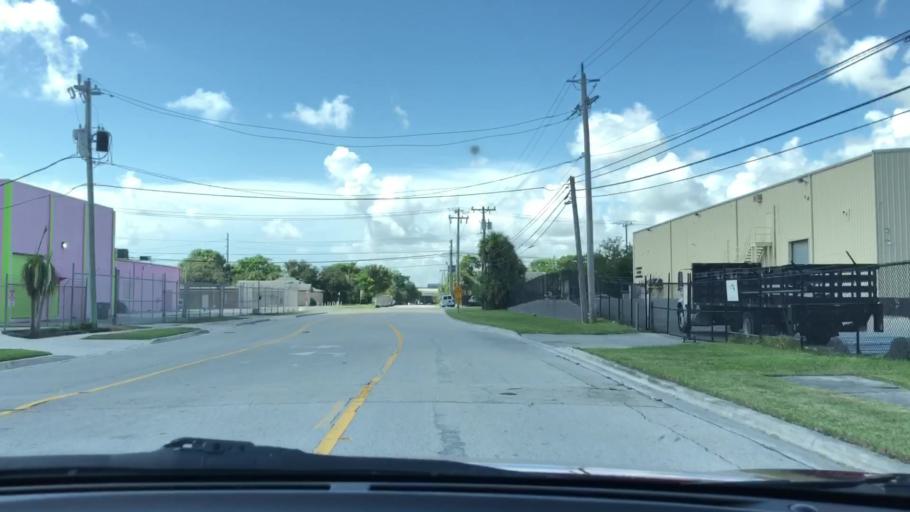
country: US
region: Florida
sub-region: Palm Beach County
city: West Palm Beach
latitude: 26.7004
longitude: -80.0677
